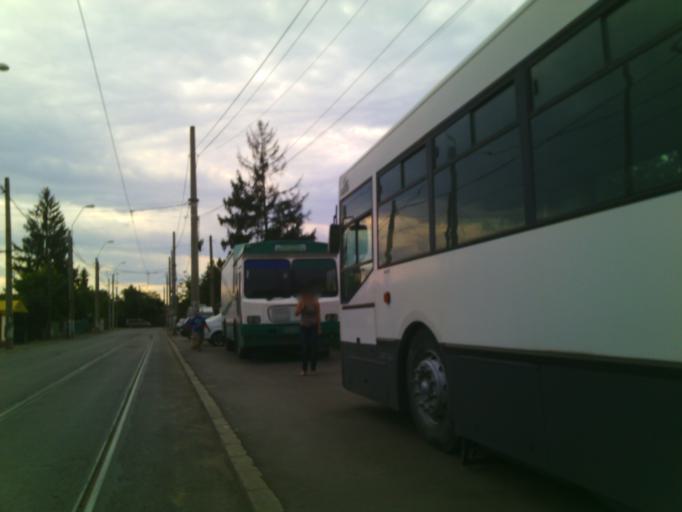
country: RO
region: Ilfov
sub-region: Comuna Jilava
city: Jilava
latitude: 44.3726
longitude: 26.0939
